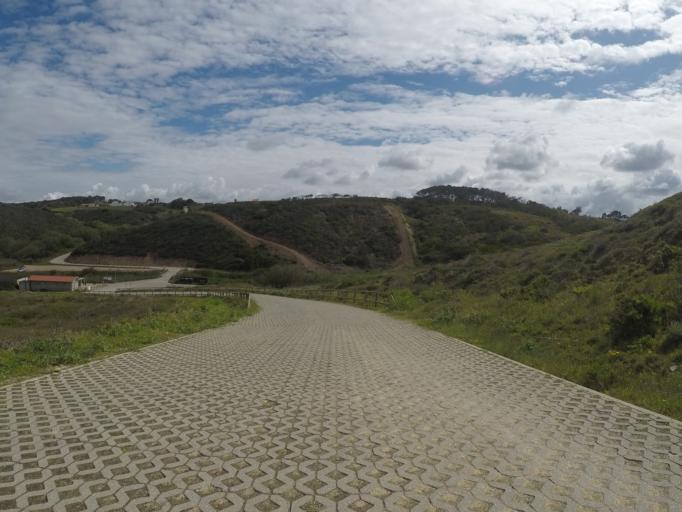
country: PT
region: Beja
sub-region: Odemira
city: Sao Teotonio
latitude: 37.4986
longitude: -8.7905
